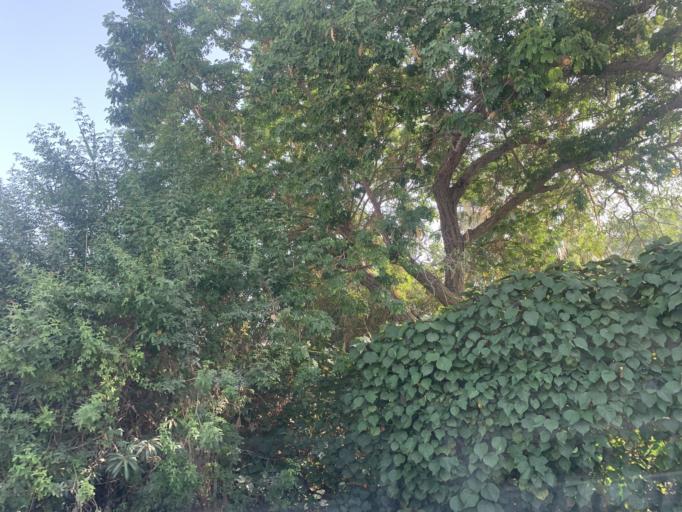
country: BH
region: Northern
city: Madinat `Isa
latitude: 26.1947
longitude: 50.4595
